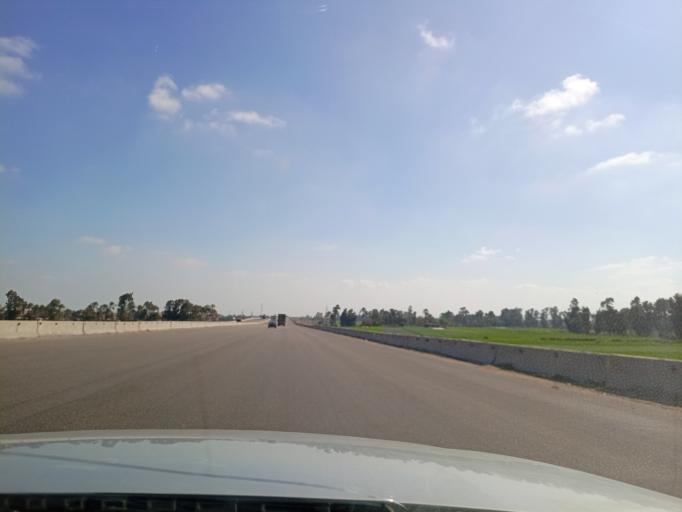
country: EG
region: Eastern Province
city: Mashtul as Suq
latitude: 30.4635
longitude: 31.3175
